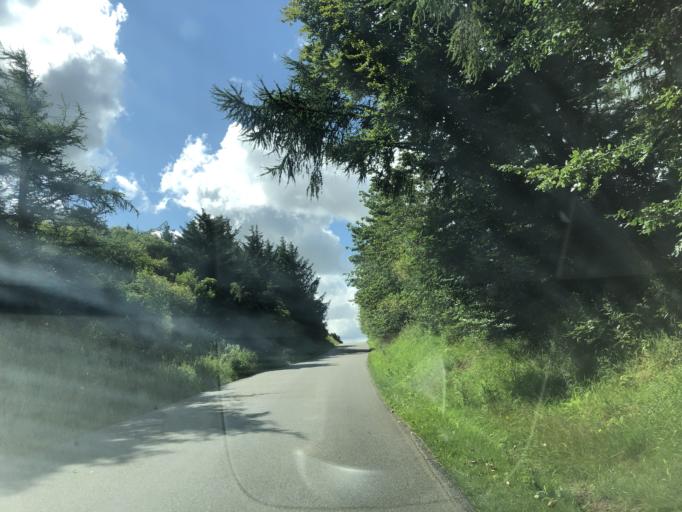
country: DK
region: Central Jutland
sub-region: Struer Kommune
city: Struer
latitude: 56.4781
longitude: 8.5222
